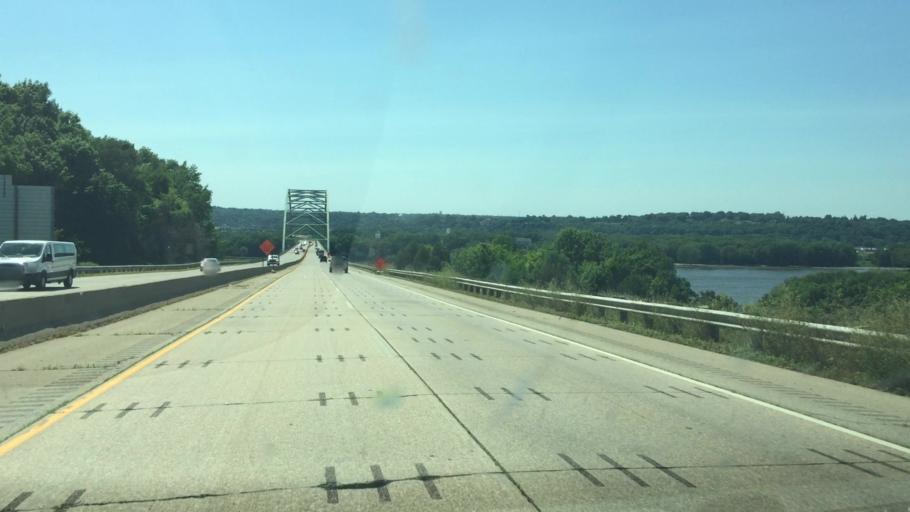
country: US
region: Illinois
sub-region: Jo Daviess County
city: East Dubuque
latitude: 42.5155
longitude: -90.6284
